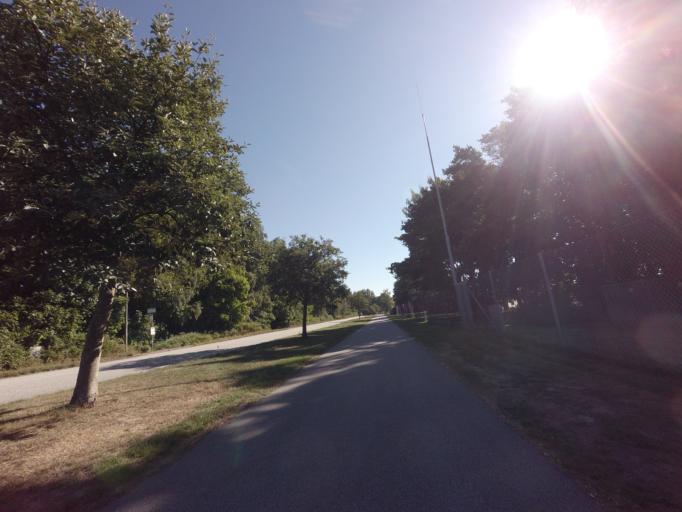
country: SE
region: Skane
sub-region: Ystads Kommun
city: Ystad
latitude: 55.4229
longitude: 13.8416
